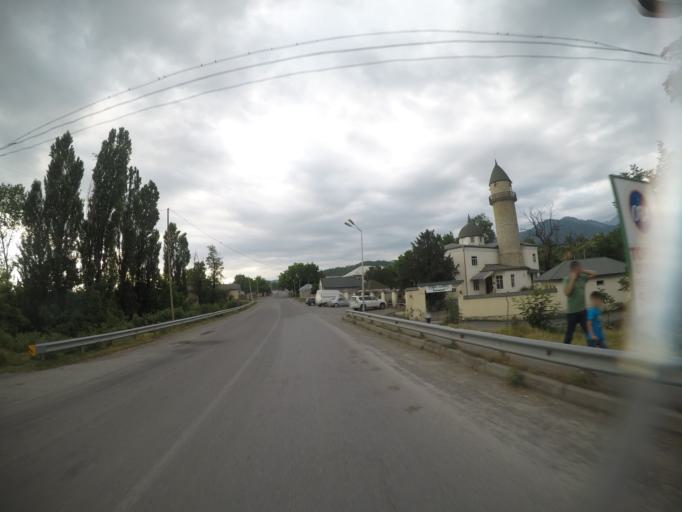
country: AZ
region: Qabala Rayon
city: Qutqashen
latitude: 40.9467
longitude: 47.9418
